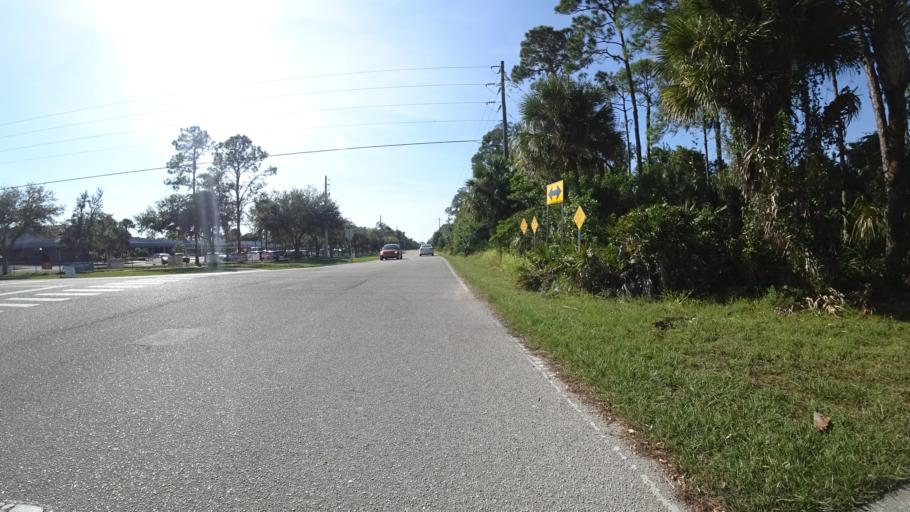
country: US
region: Florida
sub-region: Sarasota County
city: Desoto Lakes
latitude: 27.4325
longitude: -82.4710
